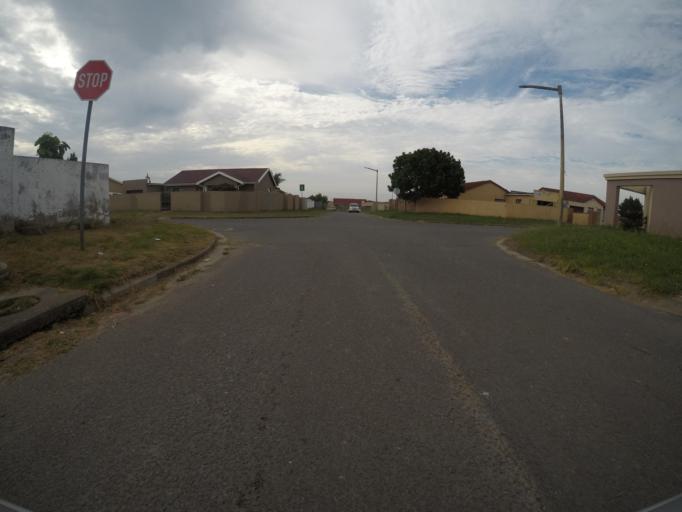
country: ZA
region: Eastern Cape
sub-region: Buffalo City Metropolitan Municipality
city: East London
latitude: -32.9775
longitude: 27.8595
